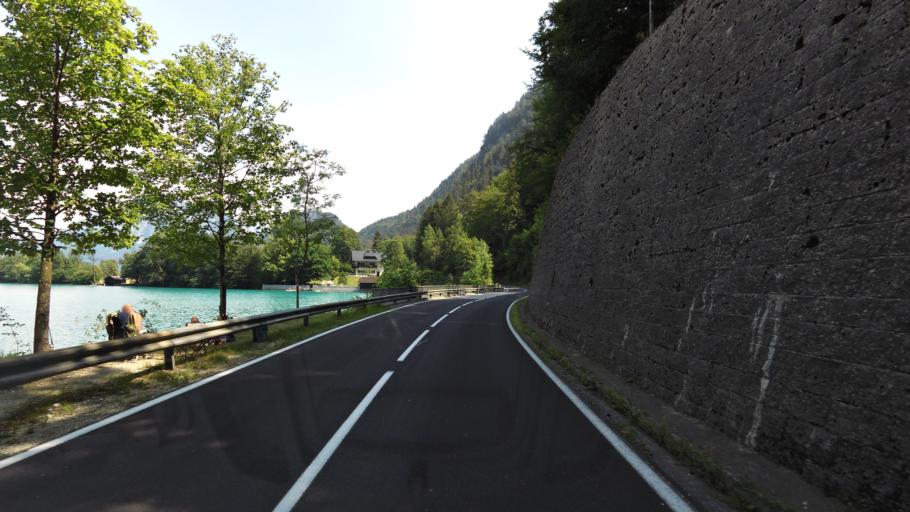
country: AT
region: Upper Austria
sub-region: Politischer Bezirk Gmunden
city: Sankt Wolfgang im Salzkammergut
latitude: 47.7895
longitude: 13.4886
